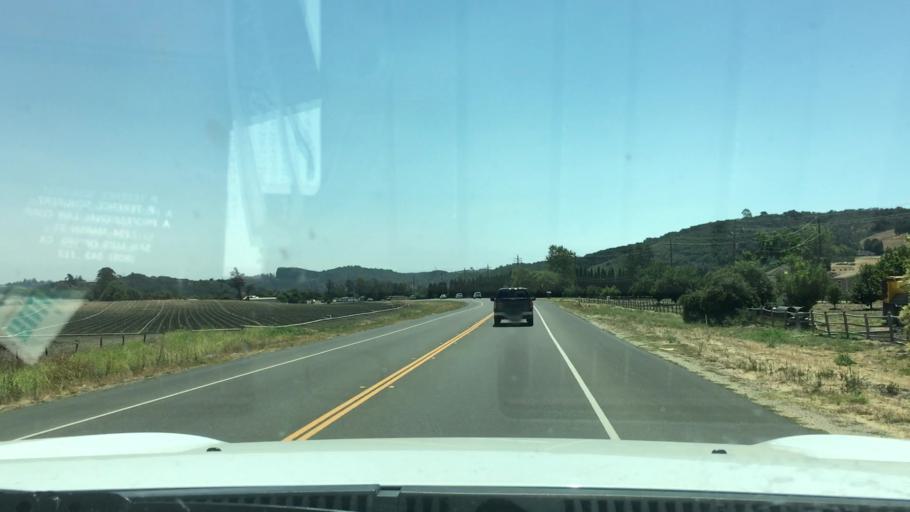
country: US
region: California
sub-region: San Luis Obispo County
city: Pismo Beach
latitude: 35.2120
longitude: -120.6161
